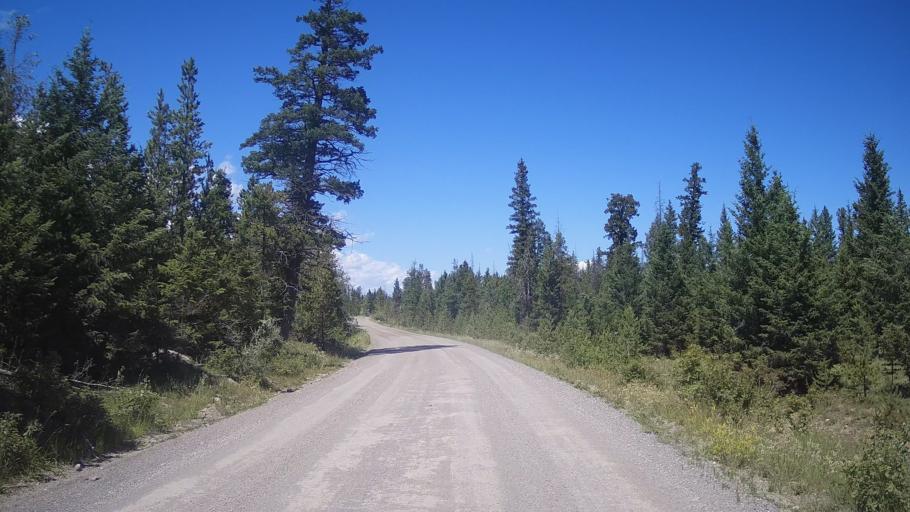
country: CA
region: British Columbia
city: Cache Creek
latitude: 51.1691
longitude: -121.5653
